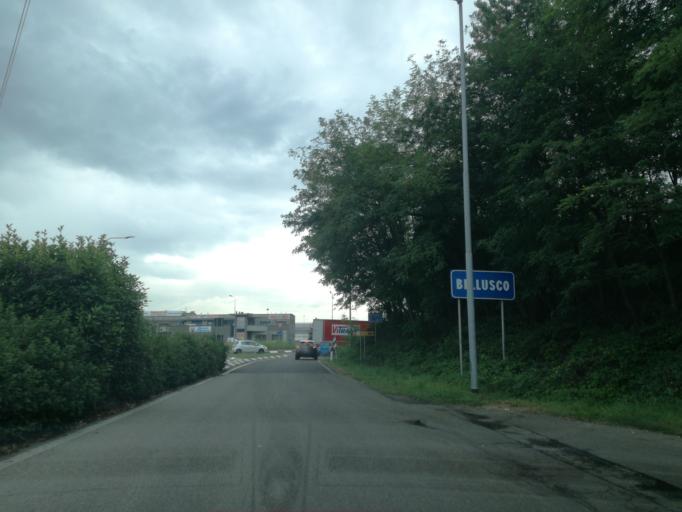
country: IT
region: Lombardy
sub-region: Provincia di Monza e Brianza
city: Mezzago
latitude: 45.6166
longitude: 9.4386
